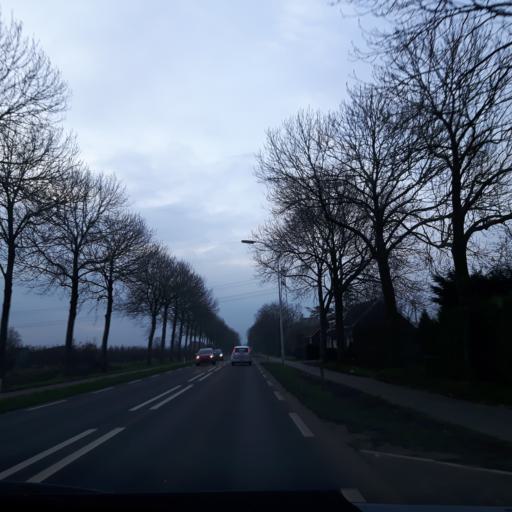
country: NL
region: Zeeland
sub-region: Gemeente Goes
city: Goes
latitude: 51.4755
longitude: 3.9033
